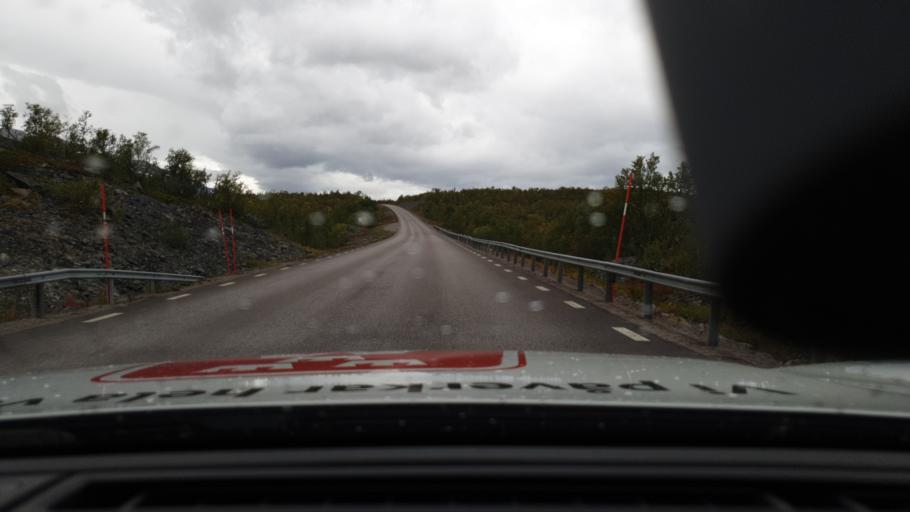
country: NO
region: Troms
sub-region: Bardu
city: Setermoen
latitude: 68.4432
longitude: 18.6096
